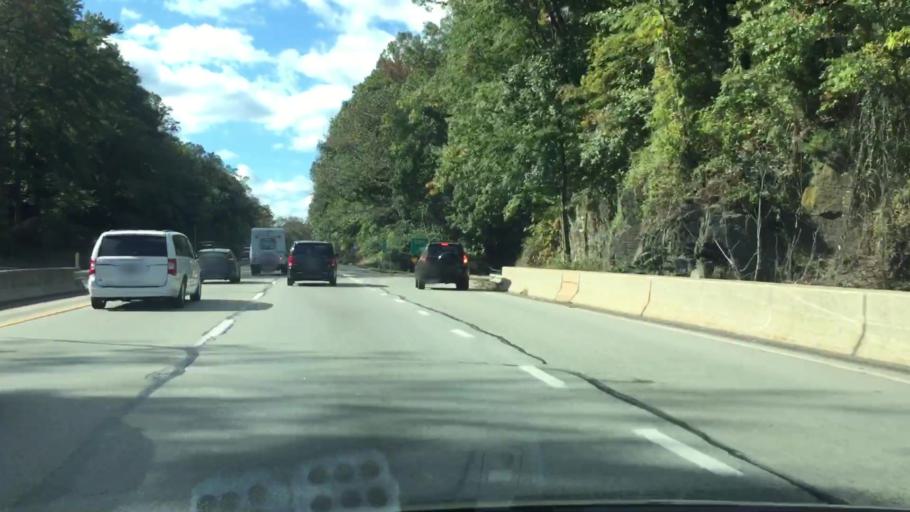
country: US
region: Pennsylvania
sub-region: Delaware County
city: Media
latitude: 39.9369
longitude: -75.3739
